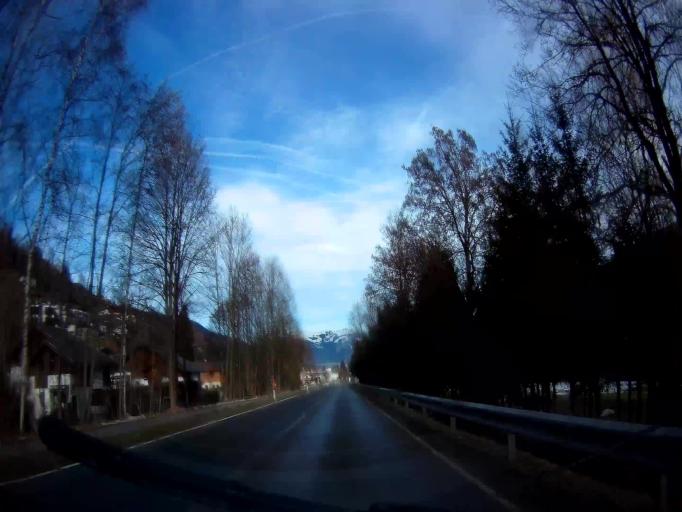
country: AT
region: Salzburg
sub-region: Politischer Bezirk Zell am See
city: Kaprun
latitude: 47.2653
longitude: 12.7468
